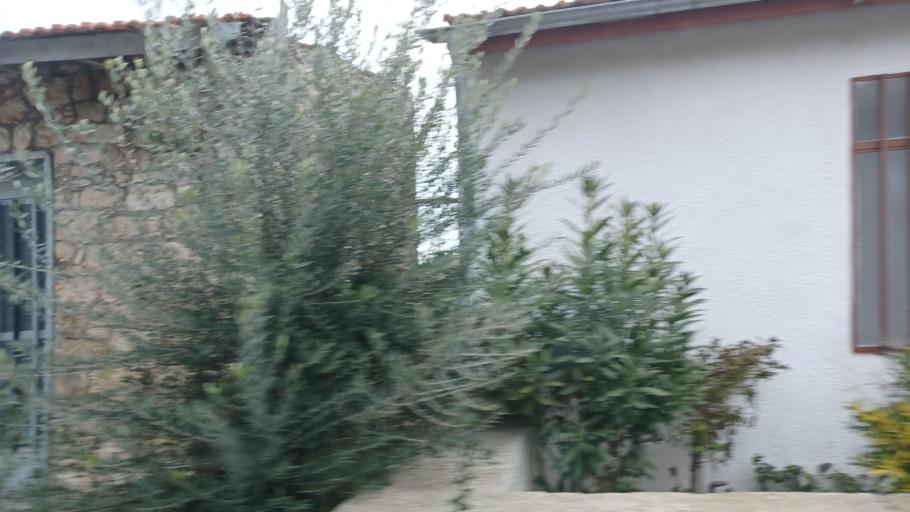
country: CY
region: Limassol
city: Pachna
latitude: 34.7379
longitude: 32.7338
